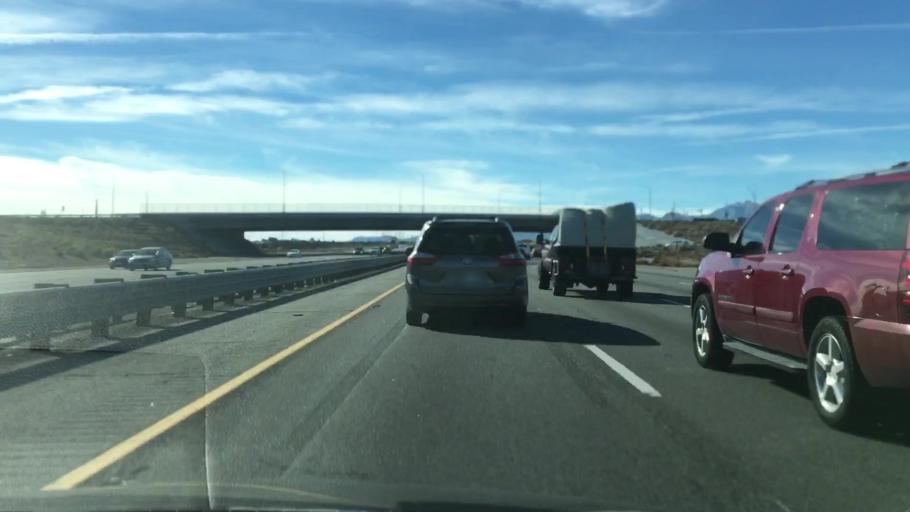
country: US
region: California
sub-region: San Bernardino County
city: Oak Hills
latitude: 34.3848
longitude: -117.4138
